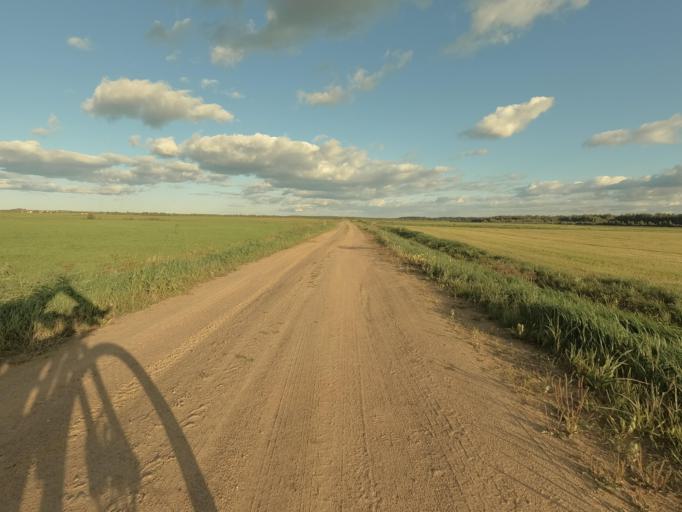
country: RU
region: Leningrad
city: Imeni Sverdlova
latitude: 59.8634
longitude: 30.7426
